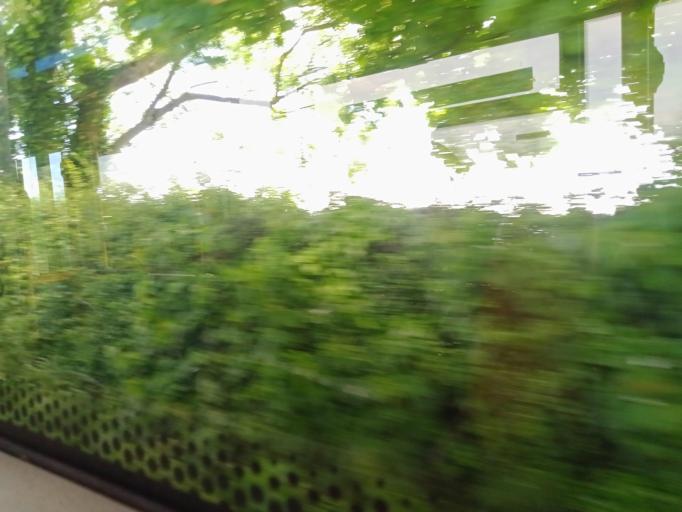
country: GB
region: Wales
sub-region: Gwynedd
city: Bangor
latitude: 53.2524
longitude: -4.1409
